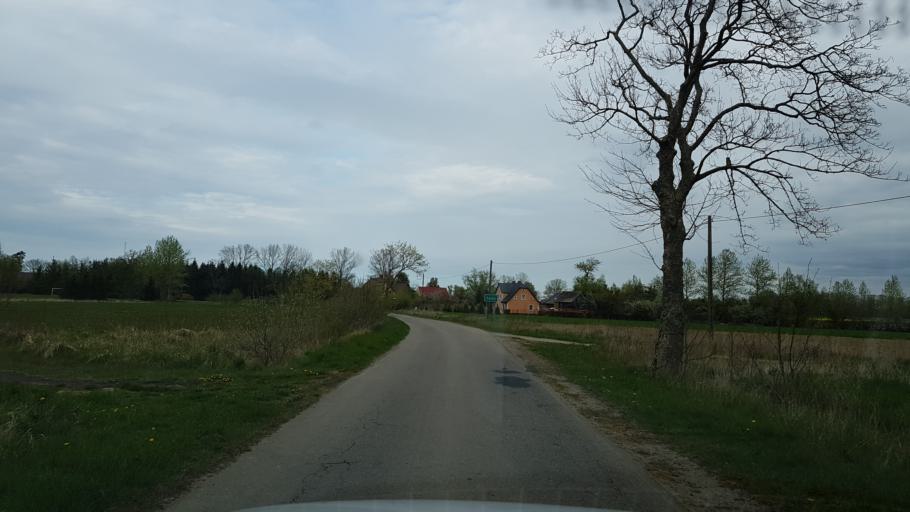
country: PL
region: West Pomeranian Voivodeship
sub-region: Powiat slawienski
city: Slawno
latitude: 54.5151
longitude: 16.6064
